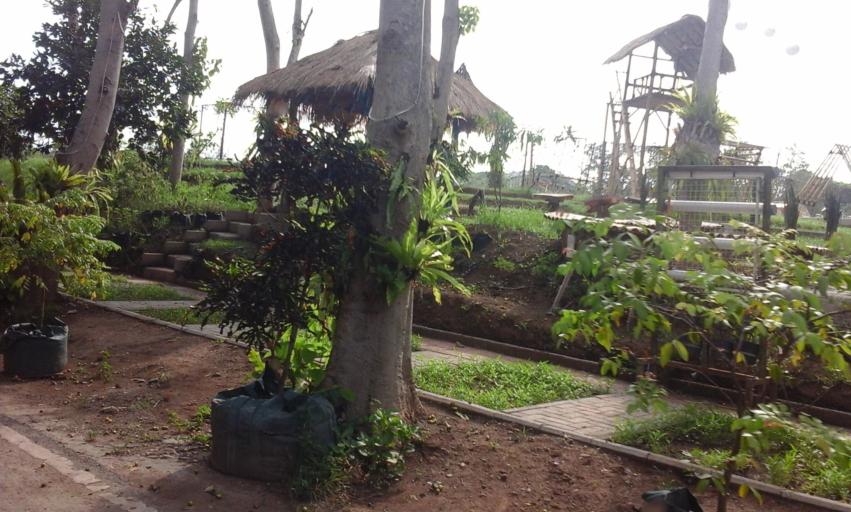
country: ID
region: East Java
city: Krajan Satu
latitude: -8.2102
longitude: 114.3538
